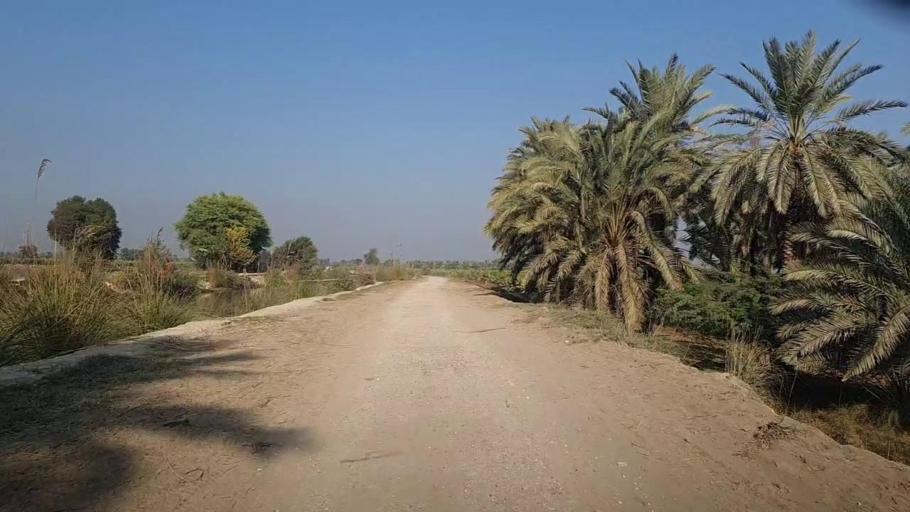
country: PK
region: Sindh
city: Ranipur
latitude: 27.2460
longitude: 68.5539
